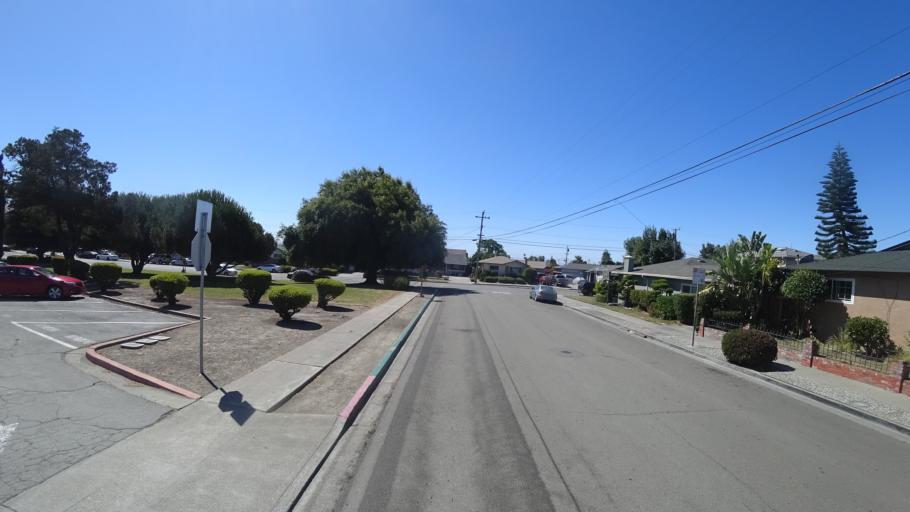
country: US
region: California
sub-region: Alameda County
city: Hayward
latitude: 37.6534
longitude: -122.0941
